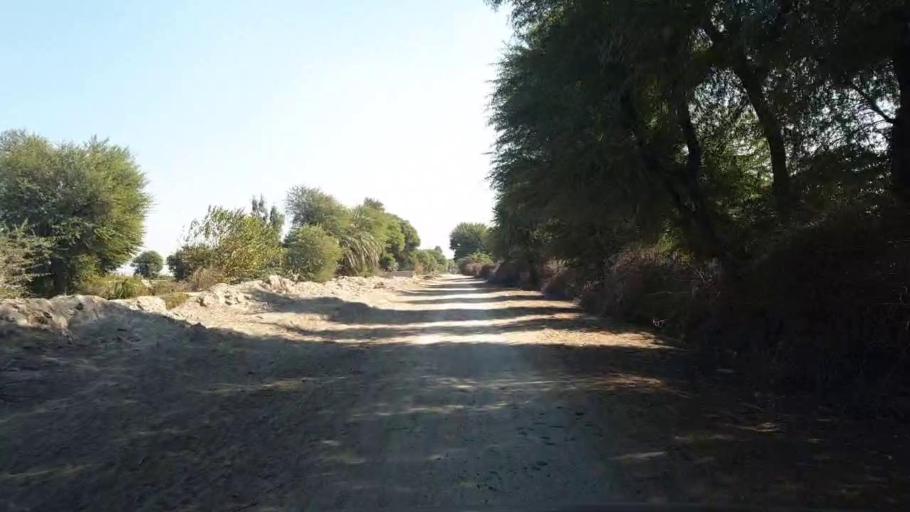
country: PK
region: Sindh
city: Shahpur Chakar
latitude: 26.1412
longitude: 68.6550
